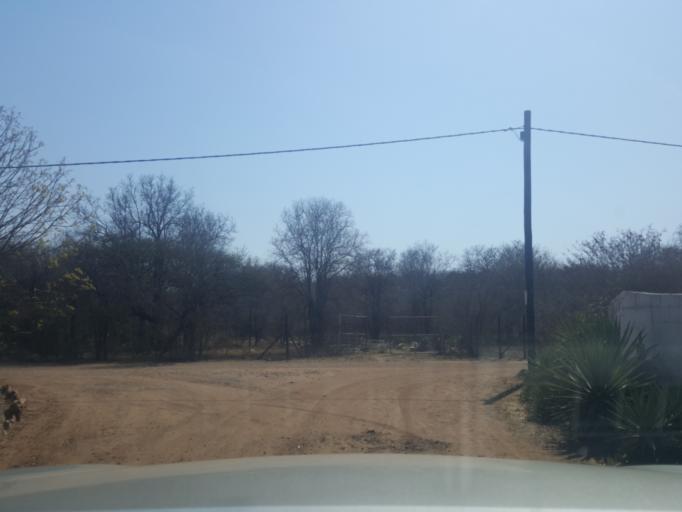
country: BW
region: Kweneng
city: Gabane
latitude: -24.7422
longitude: 25.8285
